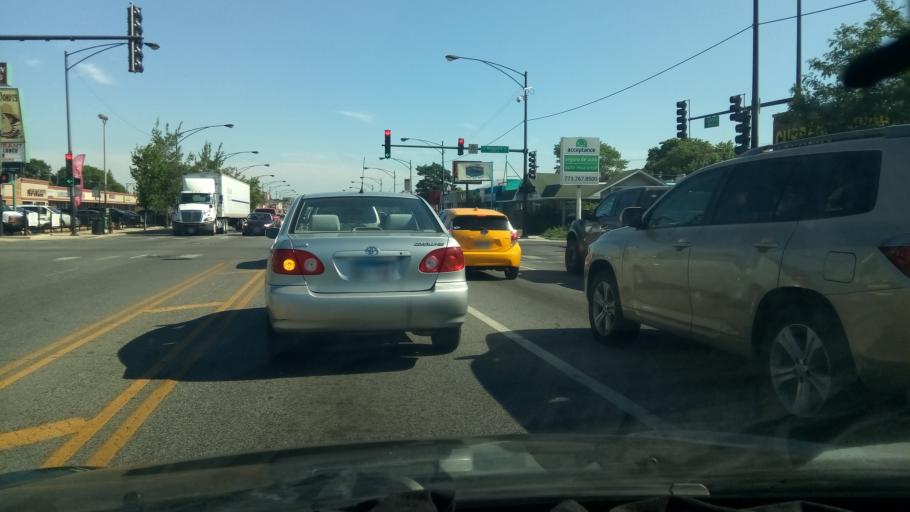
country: US
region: Illinois
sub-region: Cook County
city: Hometown
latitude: 41.7710
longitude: -87.7226
